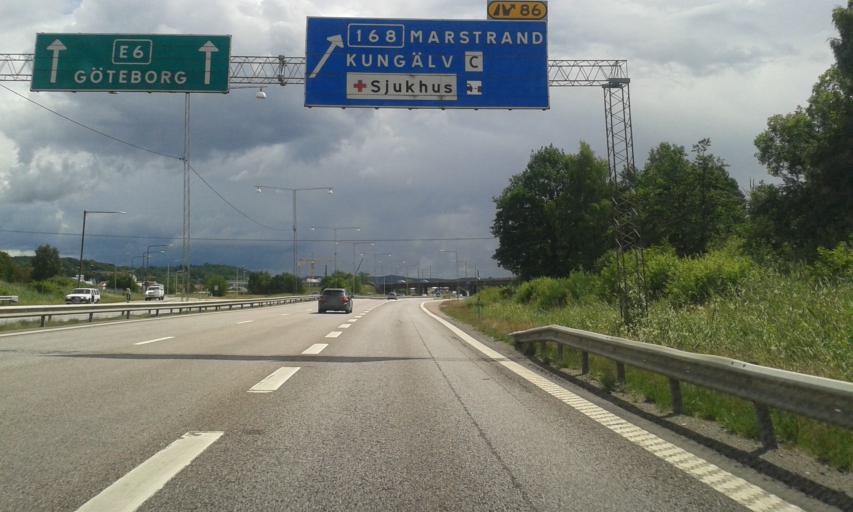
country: SE
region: Vaestra Goetaland
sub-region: Kungalvs Kommun
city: Kungalv
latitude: 57.8779
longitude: 11.9587
